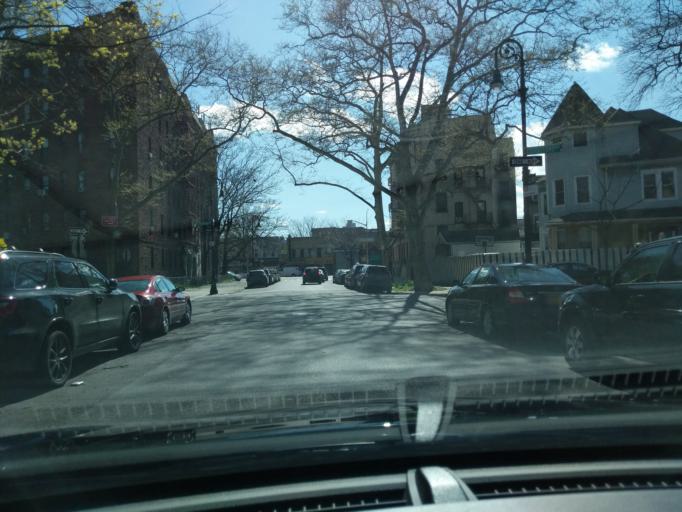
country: US
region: New York
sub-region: Kings County
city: Brooklyn
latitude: 40.6378
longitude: -73.9671
